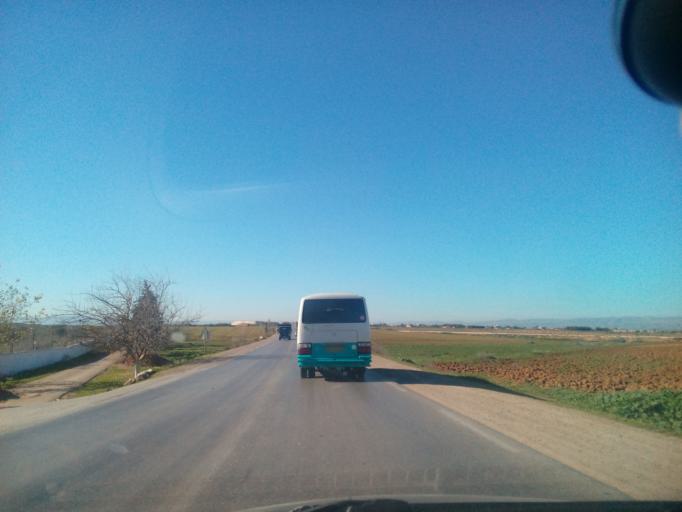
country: DZ
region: Relizane
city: Djidiouia
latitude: 35.8944
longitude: 0.7206
